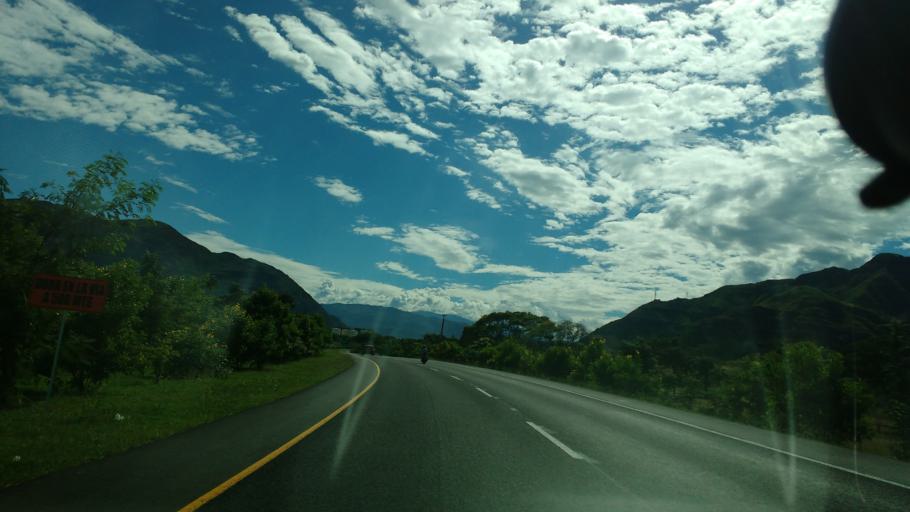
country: CO
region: Tolima
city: Valle de San Juan
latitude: 4.2777
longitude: -75.0083
